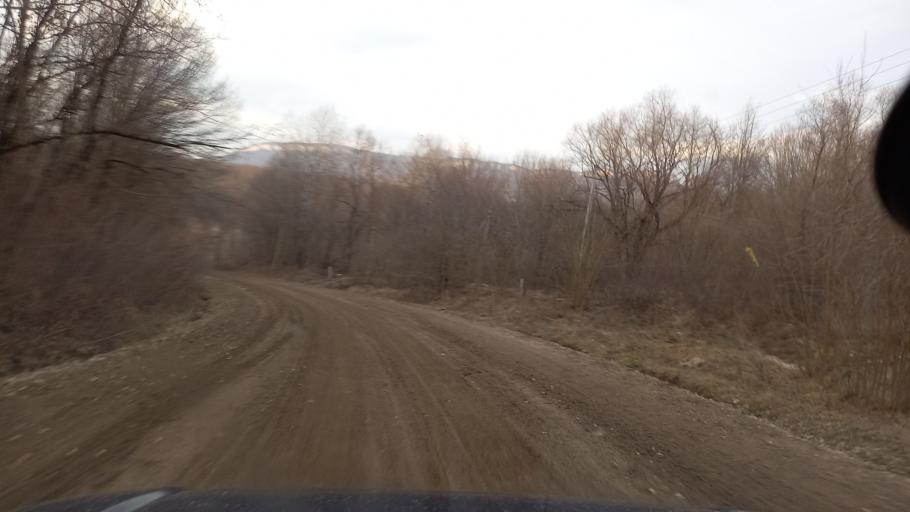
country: RU
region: Adygeya
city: Kamennomostskiy
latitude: 44.1915
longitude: 40.2601
